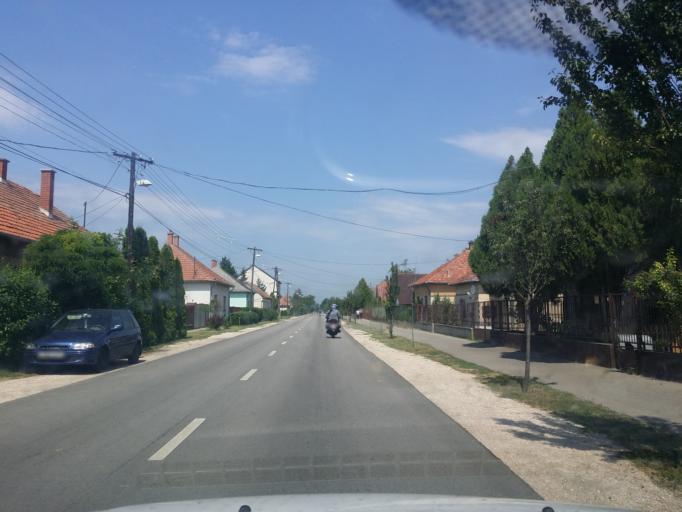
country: HU
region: Bacs-Kiskun
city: Jaszszentlaszlo
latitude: 46.5707
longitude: 19.7536
